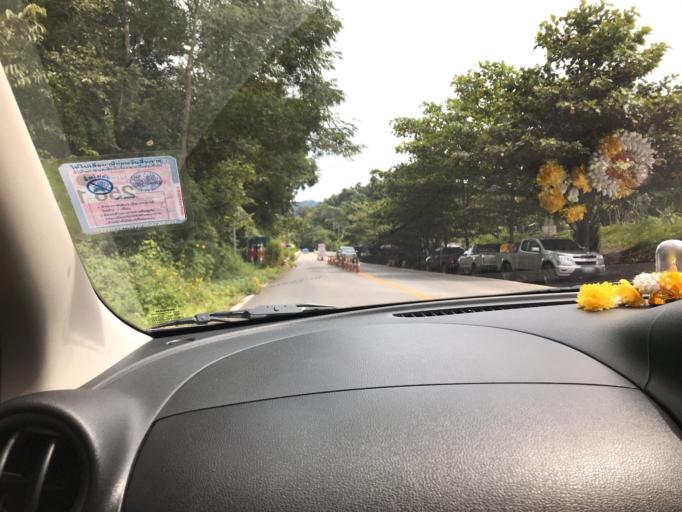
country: TH
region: Kanchanaburi
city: Sangkhla Buri
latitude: 15.1312
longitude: 98.5065
